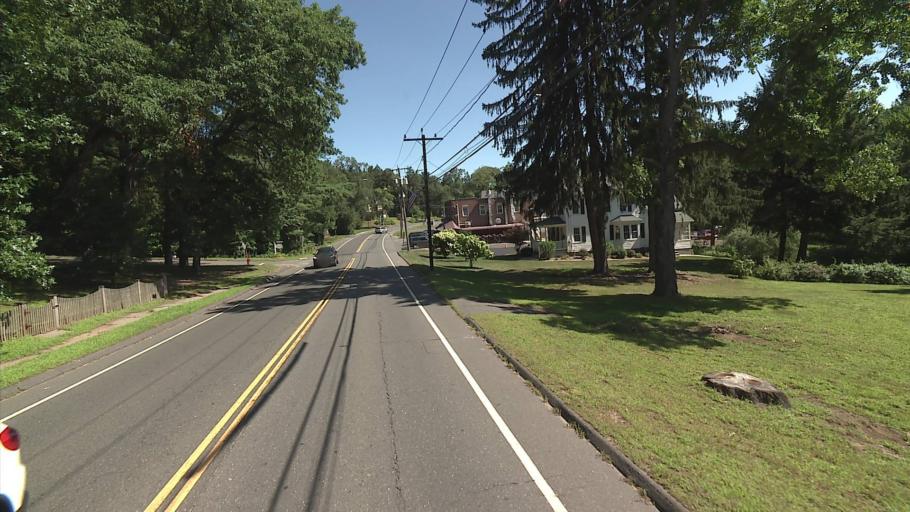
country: US
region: Connecticut
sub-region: Hartford County
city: Simsbury Center
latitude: 41.8623
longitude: -72.8099
